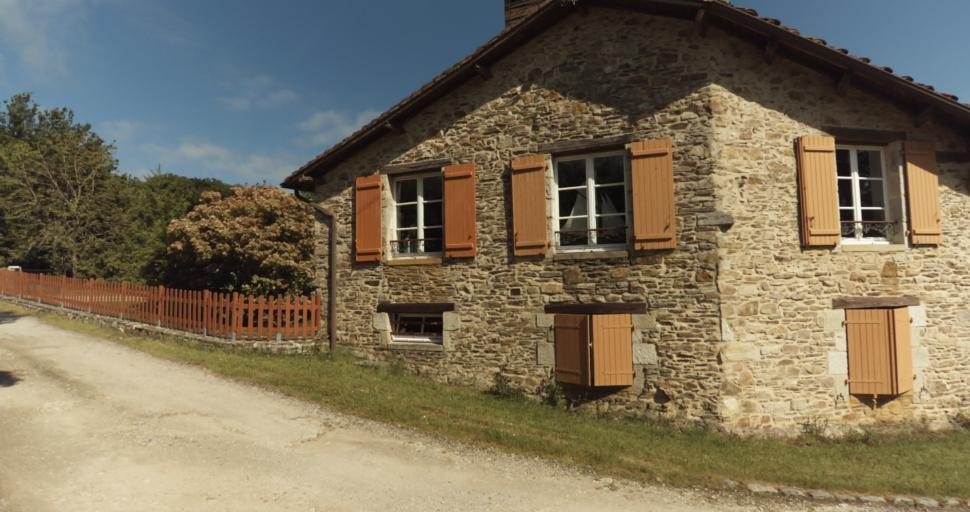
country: FR
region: Limousin
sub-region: Departement de la Haute-Vienne
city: Solignac
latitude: 45.7236
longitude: 1.2621
